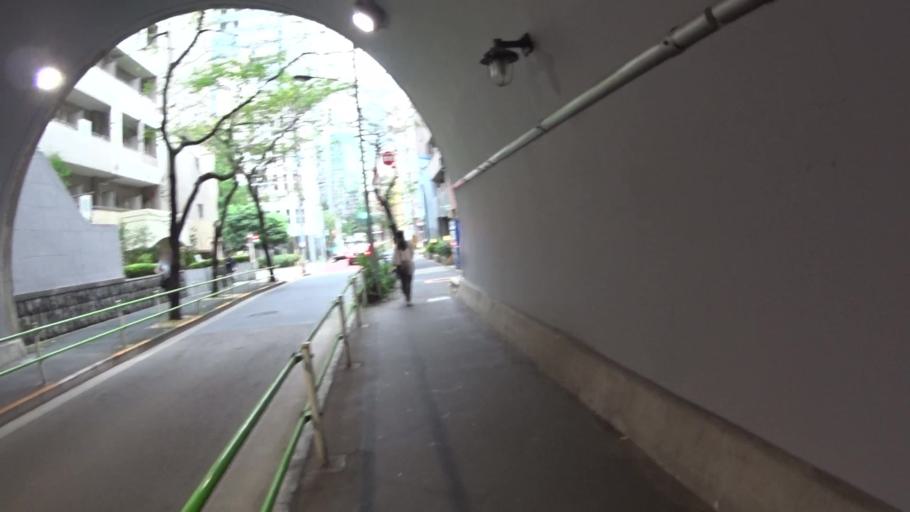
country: JP
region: Tokyo
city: Tokyo
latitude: 35.6642
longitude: 139.7489
